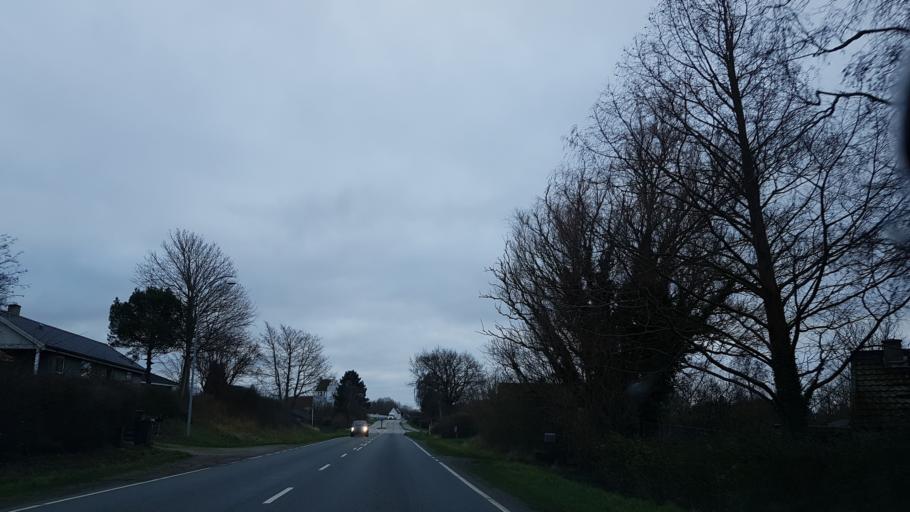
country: DK
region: Zealand
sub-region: Holbaek Kommune
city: Jyderup
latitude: 55.7194
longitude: 11.3806
